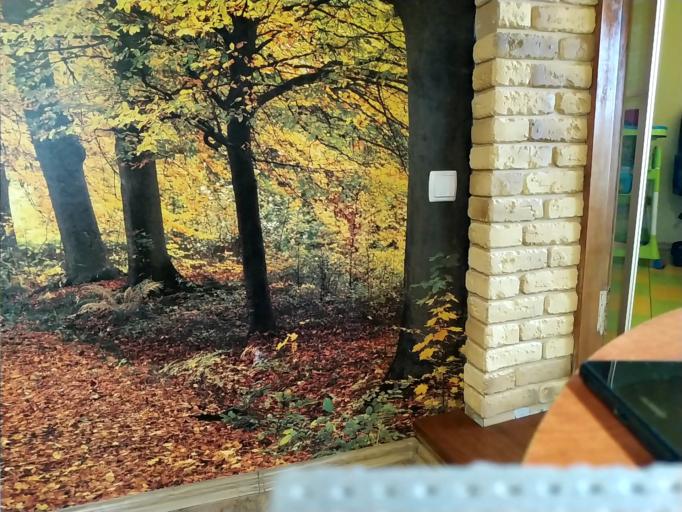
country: RU
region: Kaluga
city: Iznoski
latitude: 54.8589
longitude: 35.4382
